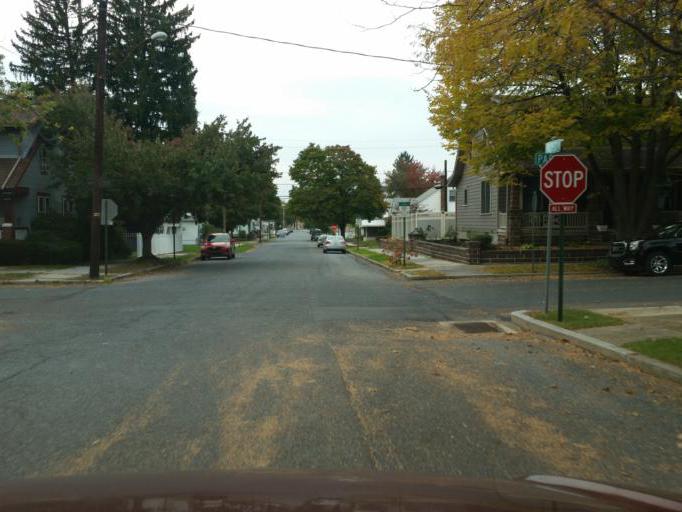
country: US
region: Pennsylvania
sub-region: Dauphin County
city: Hummelstown
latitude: 40.2620
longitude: -76.7036
